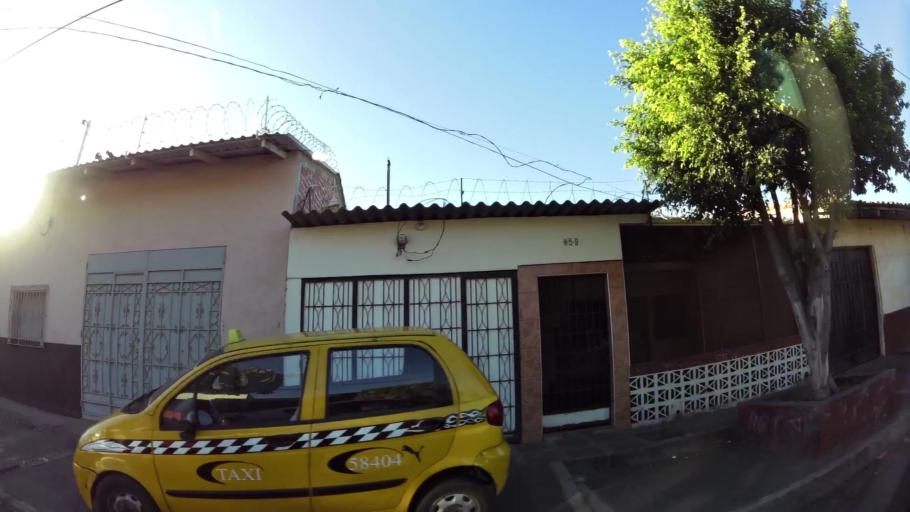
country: SV
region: San Miguel
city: San Miguel
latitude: 13.4851
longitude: -88.1681
